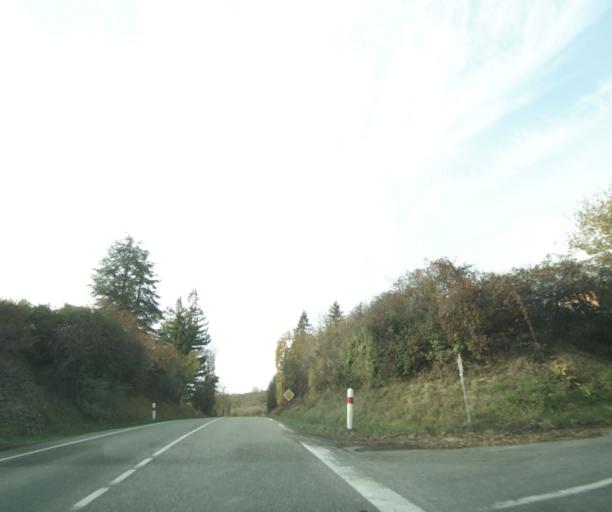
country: FR
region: Midi-Pyrenees
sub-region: Departement du Gers
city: Vic-Fezensac
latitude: 43.7481
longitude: 0.3374
